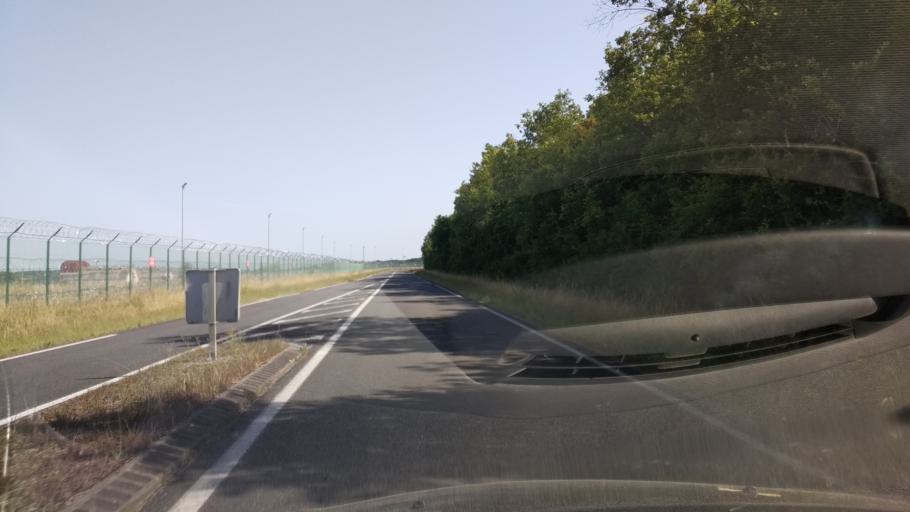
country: FR
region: Poitou-Charentes
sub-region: Departement de la Vienne
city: Lussac-les-Chateaux
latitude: 46.4574
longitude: 0.6465
